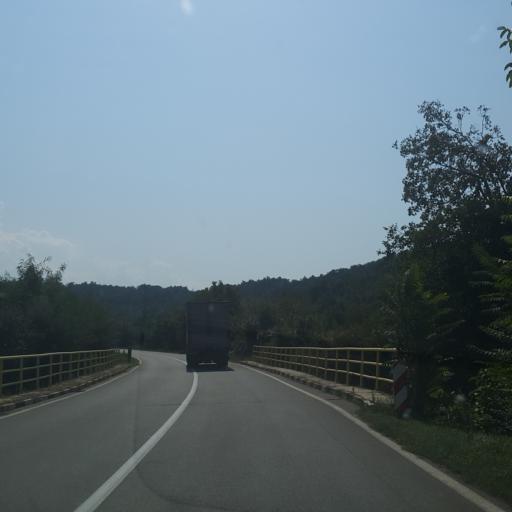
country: RS
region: Central Serbia
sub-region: Zajecarski Okrug
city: Zajecar
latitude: 43.8152
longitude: 22.2864
